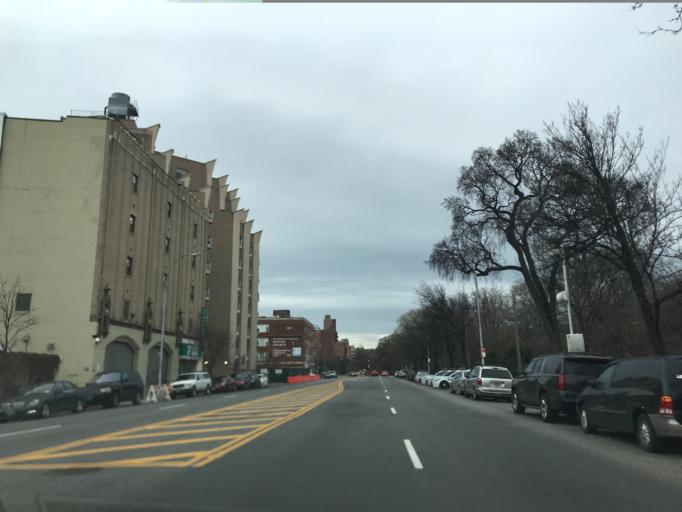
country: US
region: New York
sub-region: Kings County
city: Brooklyn
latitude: 40.6488
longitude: -73.9715
